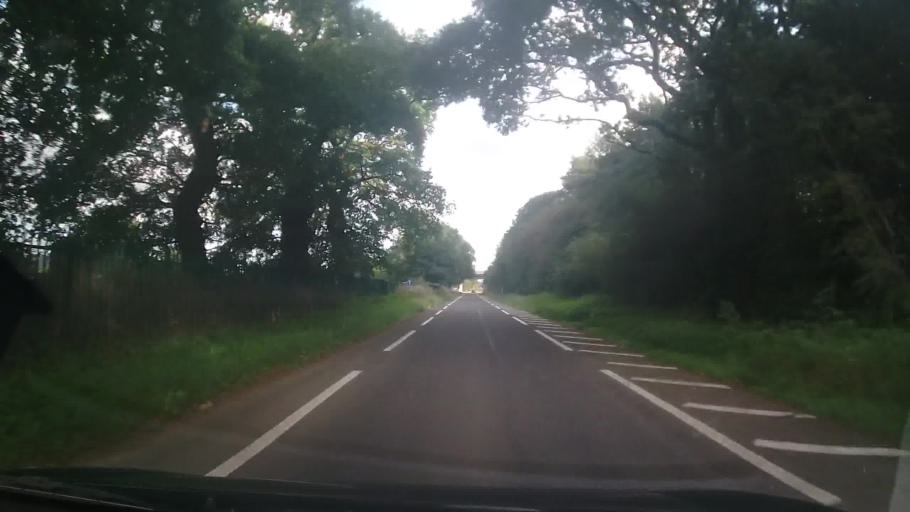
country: GB
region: England
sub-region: Shropshire
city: Ludlow
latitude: 52.3828
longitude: -2.7322
